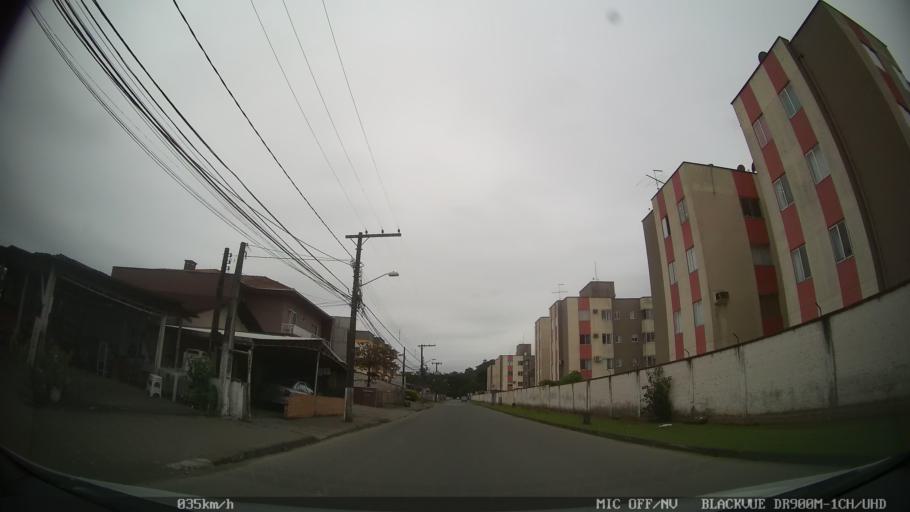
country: BR
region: Santa Catarina
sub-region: Joinville
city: Joinville
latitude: -26.2838
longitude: -48.9033
